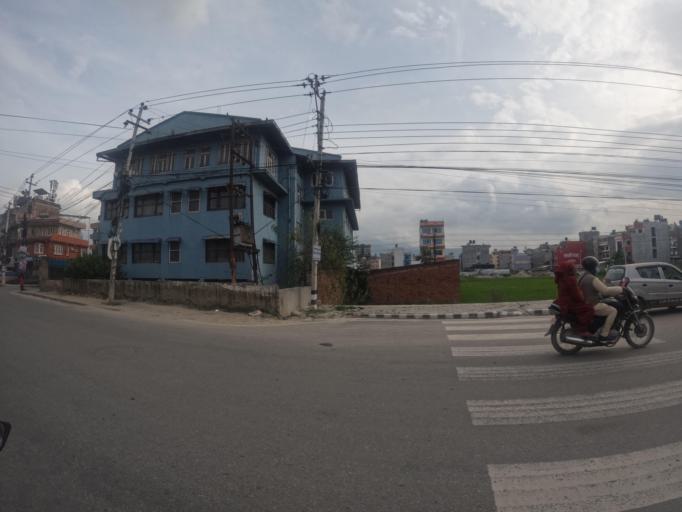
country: NP
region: Central Region
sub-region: Bagmati Zone
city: Bhaktapur
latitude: 27.6801
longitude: 85.3982
